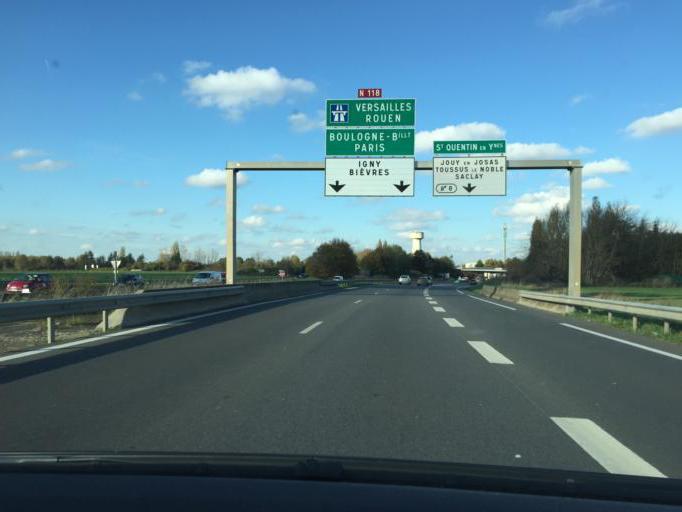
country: FR
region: Ile-de-France
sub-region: Departement de l'Essonne
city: Saclay
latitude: 48.7260
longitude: 2.1662
